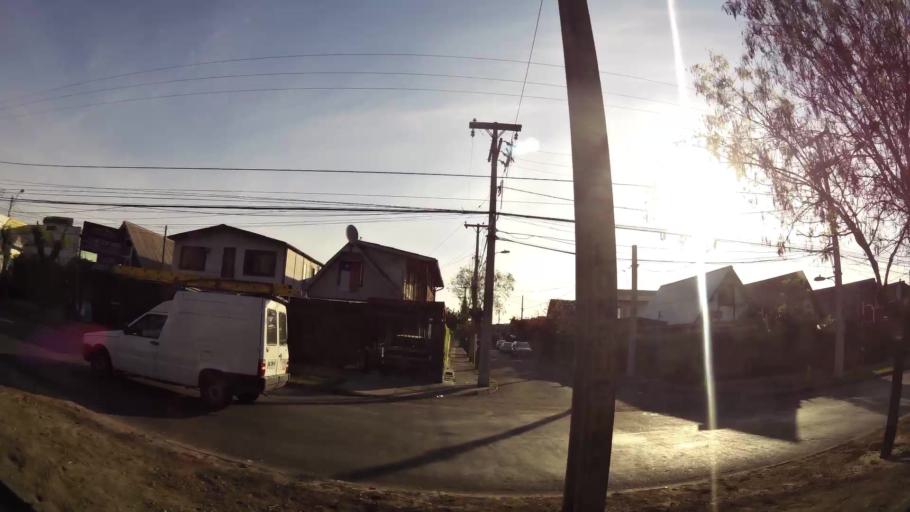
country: CL
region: Santiago Metropolitan
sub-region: Provincia de Santiago
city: Villa Presidente Frei, Nunoa, Santiago, Chile
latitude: -33.5307
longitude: -70.5754
